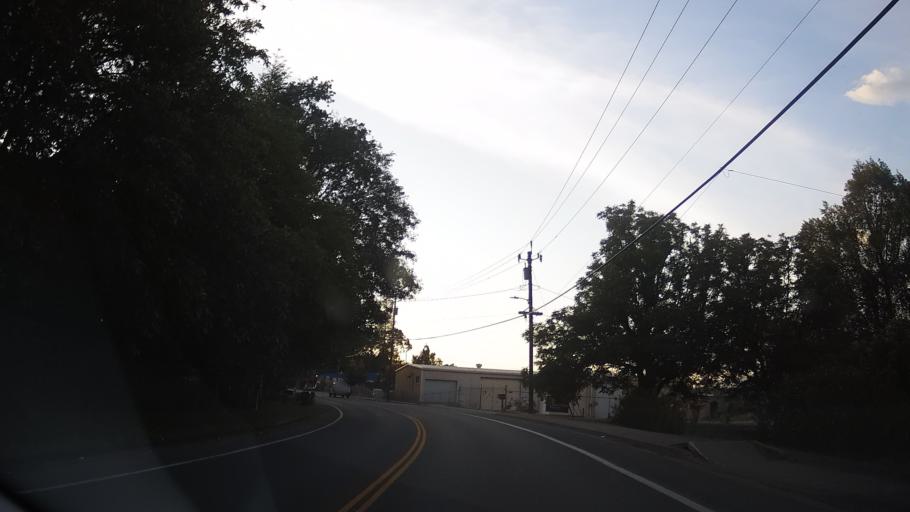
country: US
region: California
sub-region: Mendocino County
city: Willits
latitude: 39.3961
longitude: -123.3449
